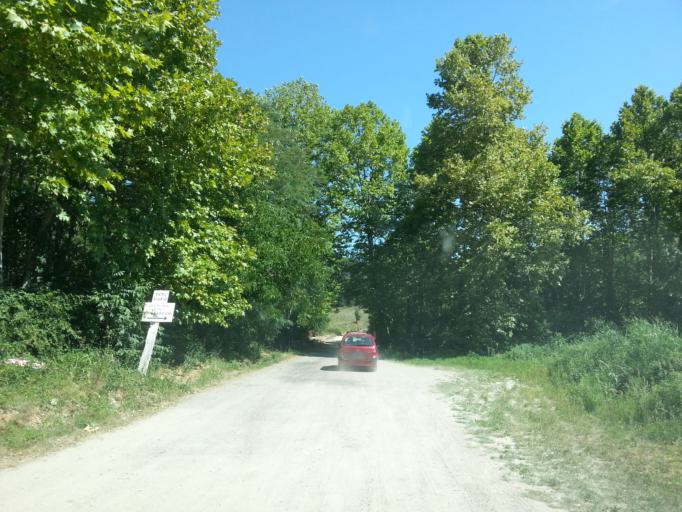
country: ES
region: Catalonia
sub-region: Provincia de Barcelona
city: Campins
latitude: 41.7250
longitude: 2.5137
